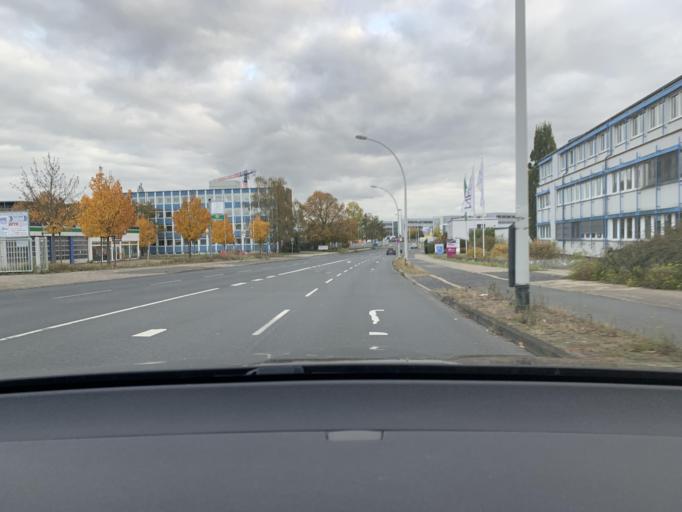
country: DE
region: Lower Saxony
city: Braunschweig
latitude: 52.2990
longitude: 10.5103
